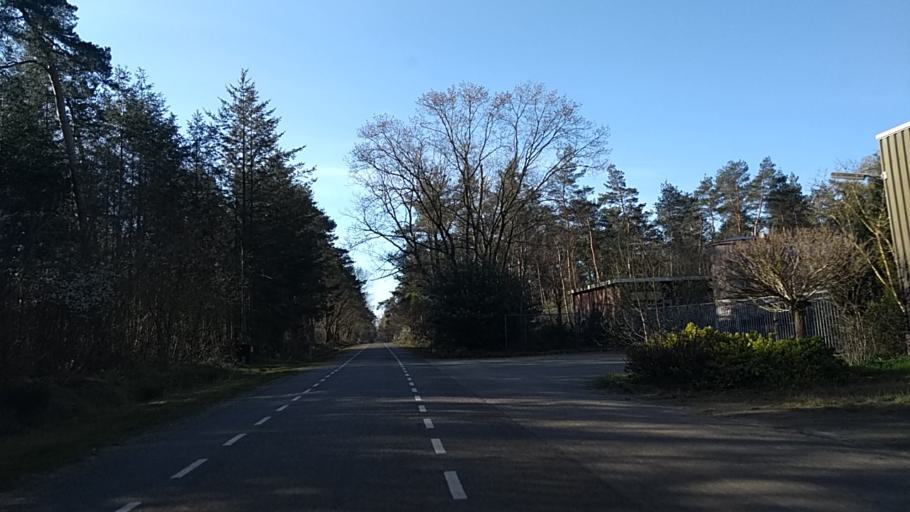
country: NL
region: Overijssel
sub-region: Gemeente Hof van Twente
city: Delden
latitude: 52.2773
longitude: 6.6688
